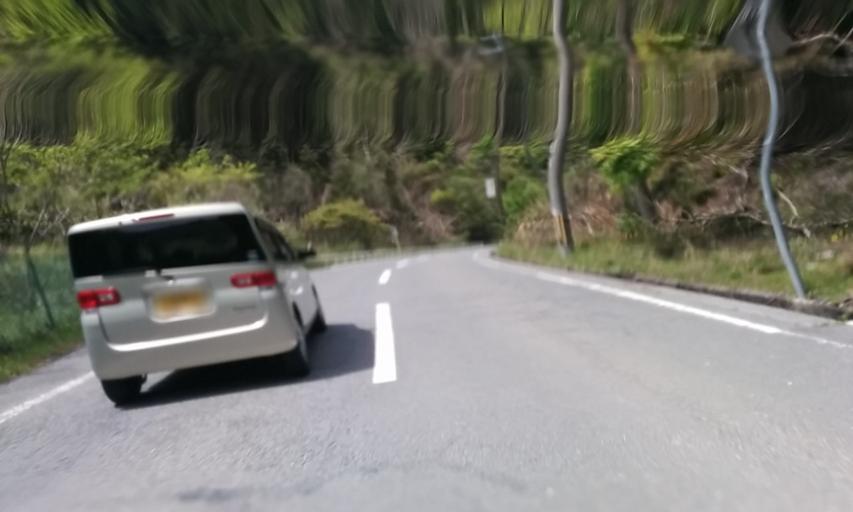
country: JP
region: Osaka
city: Takatsuki
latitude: 34.9208
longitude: 135.6032
